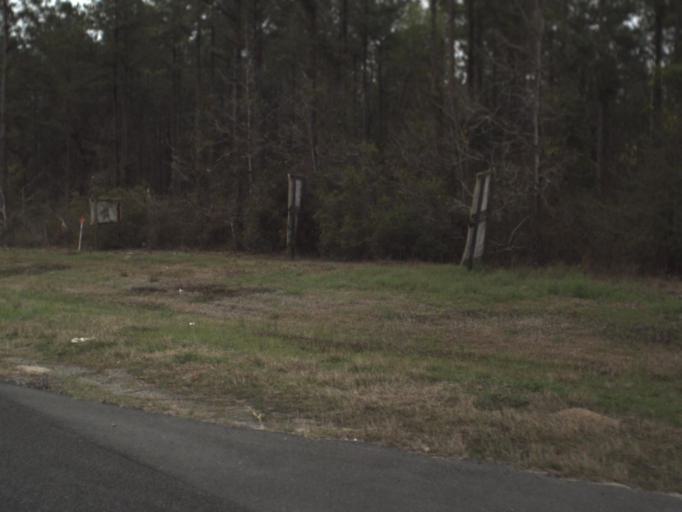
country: US
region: Florida
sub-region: Jefferson County
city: Monticello
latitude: 30.3890
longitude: -83.8566
